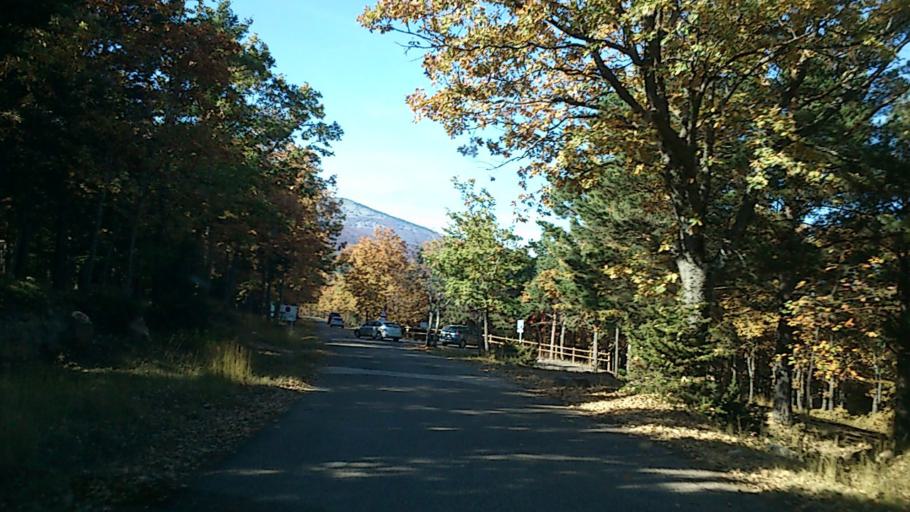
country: ES
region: Aragon
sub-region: Provincia de Zaragoza
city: Litago
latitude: 41.8066
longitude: -1.7937
